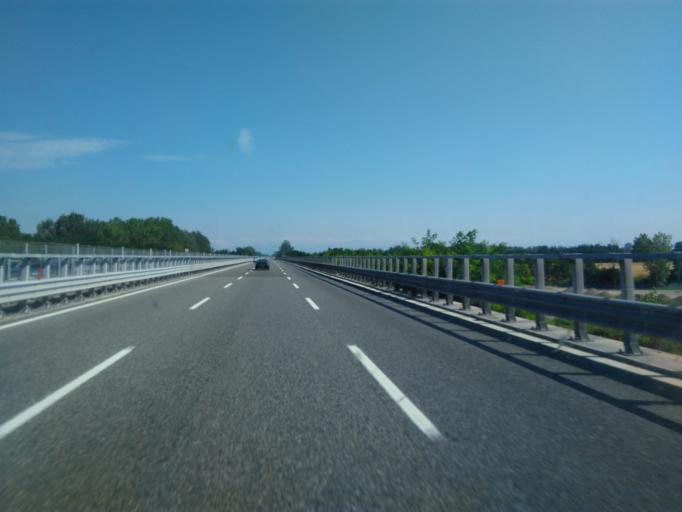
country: IT
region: Piedmont
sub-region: Provincia di Alessandria
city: Castellazzo Bormida
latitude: 44.8646
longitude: 8.5799
